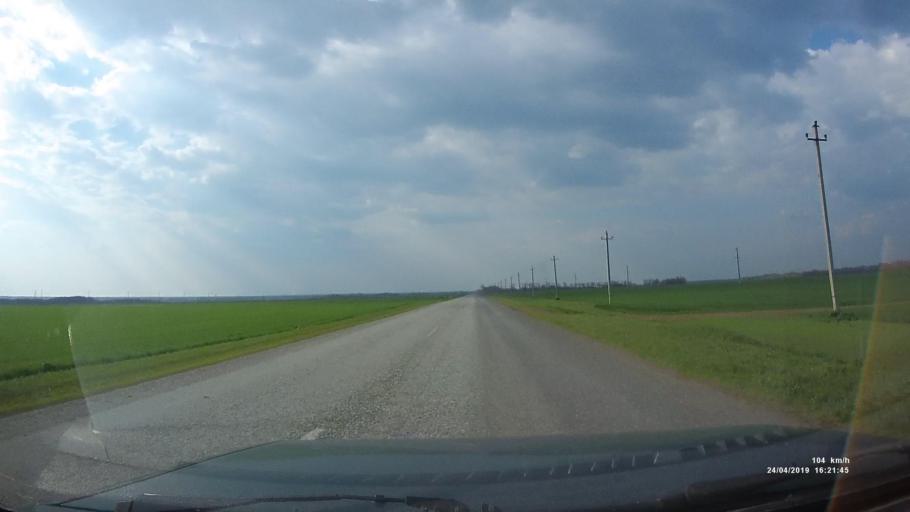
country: RU
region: Rostov
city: Orlovskiy
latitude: 46.8095
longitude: 42.0624
